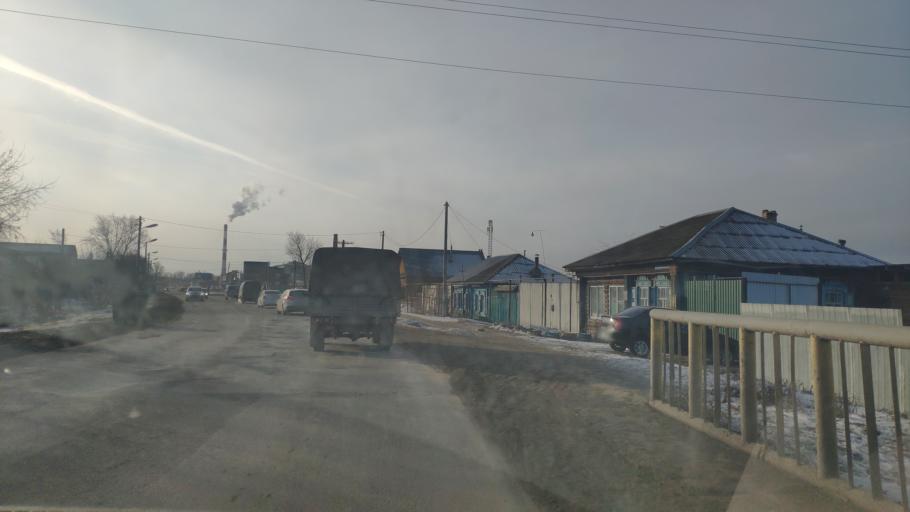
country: RU
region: Kurgan
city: Shadrinsk
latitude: 56.0895
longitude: 63.6759
